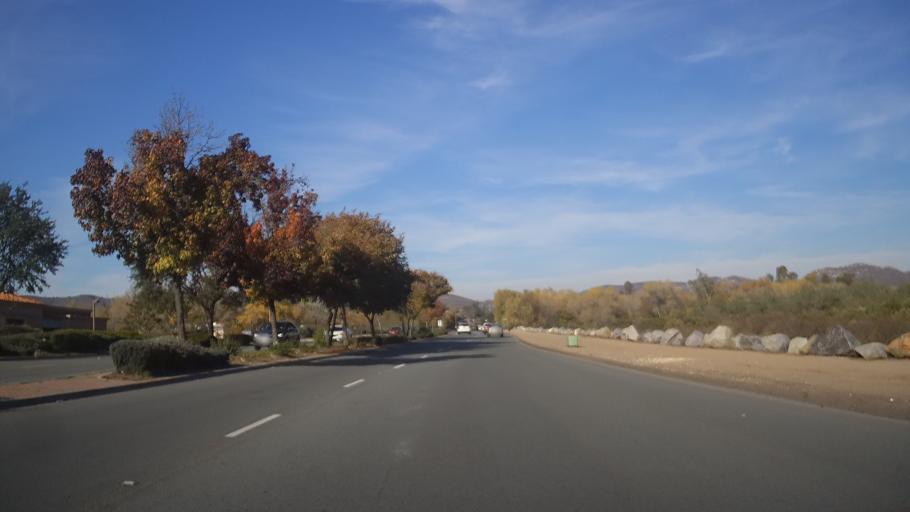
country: US
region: California
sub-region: San Diego County
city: Santee
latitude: 32.8437
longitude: -116.9837
